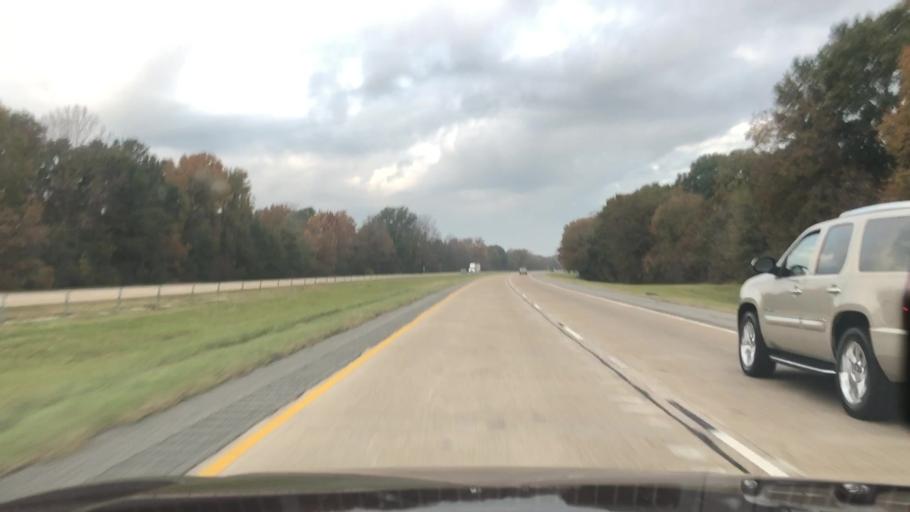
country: US
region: Louisiana
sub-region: Madison Parish
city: Tallulah
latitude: 32.3366
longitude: -91.0618
